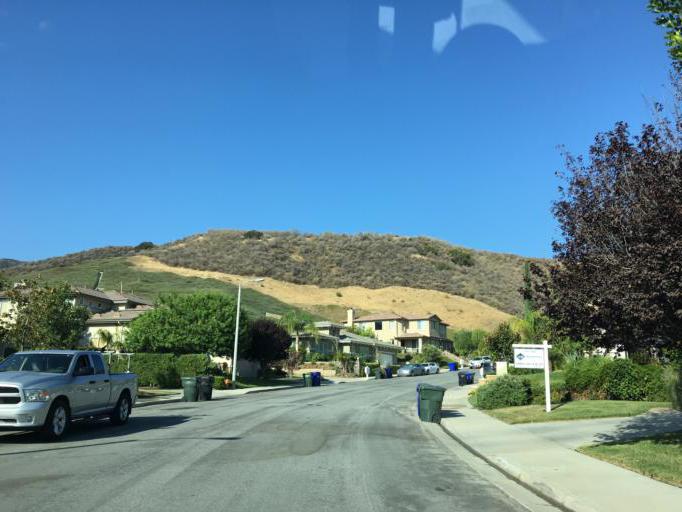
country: US
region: California
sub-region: Los Angeles County
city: Santa Clarita
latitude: 34.3747
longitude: -118.5929
